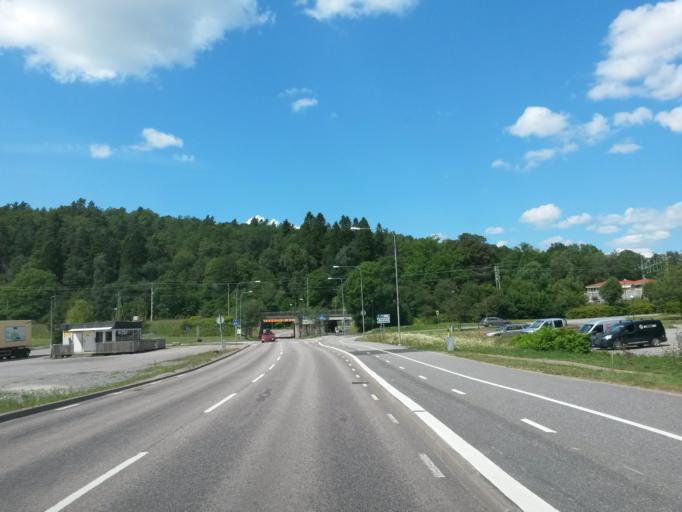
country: SE
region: Vaestra Goetaland
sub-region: Lerums Kommun
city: Stenkullen
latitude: 57.8075
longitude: 12.3587
